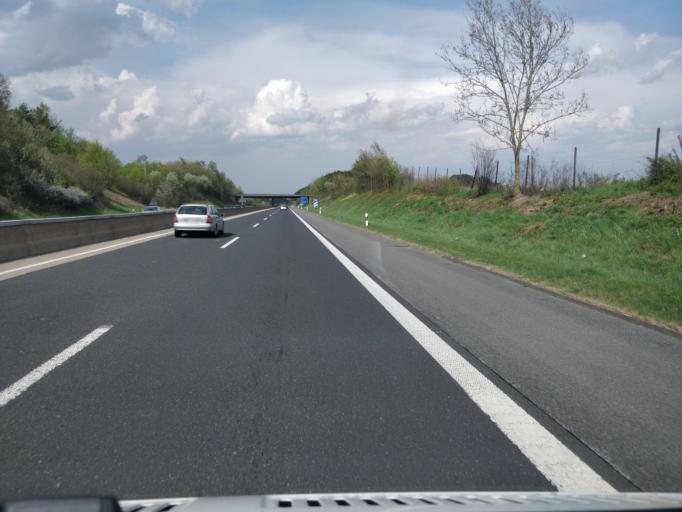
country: DE
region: North Rhine-Westphalia
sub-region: Regierungsbezirk Koln
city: Nettersheim
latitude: 50.5241
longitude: 6.6679
